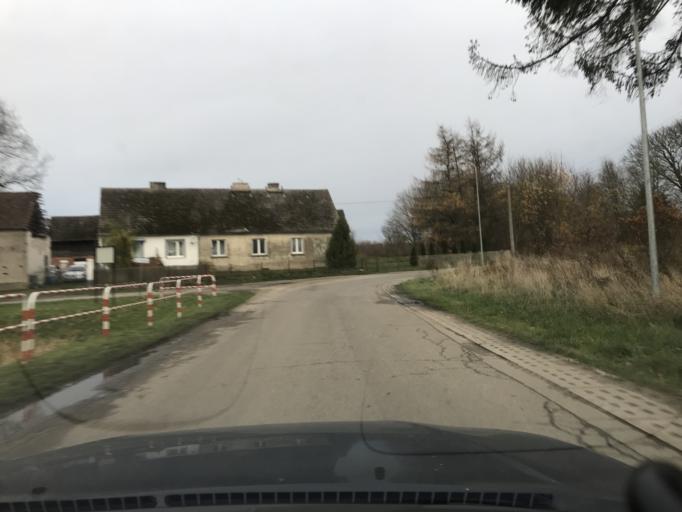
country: PL
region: Pomeranian Voivodeship
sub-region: Powiat slupski
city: Kobylnica
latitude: 54.4463
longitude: 16.8861
